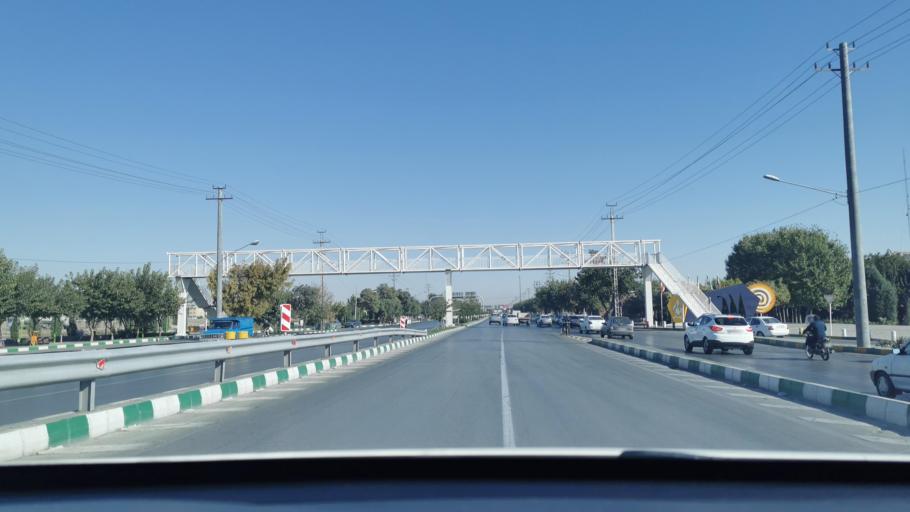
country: IR
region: Razavi Khorasan
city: Mashhad
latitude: 36.3309
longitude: 59.6248
